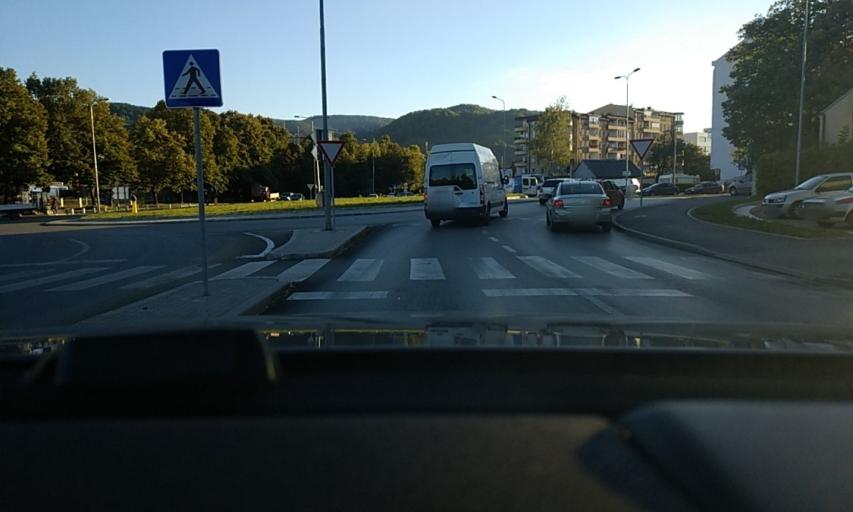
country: BA
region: Republika Srpska
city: Starcevica
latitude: 44.7668
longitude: 17.2093
